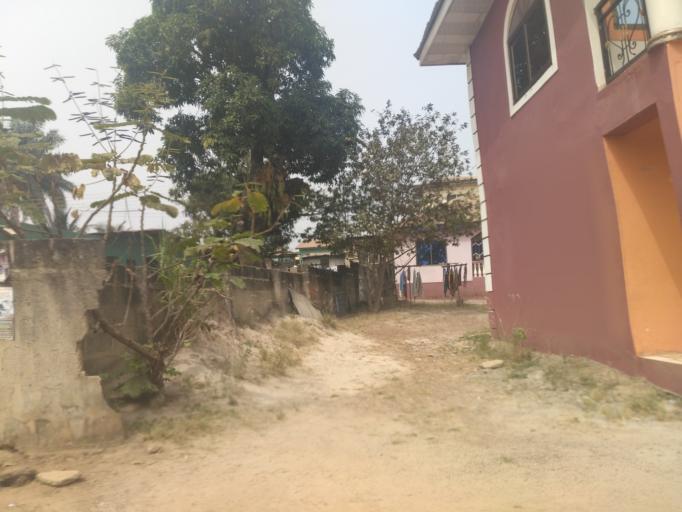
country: GH
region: Ashanti
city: Kumasi
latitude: 6.6969
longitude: -1.6388
